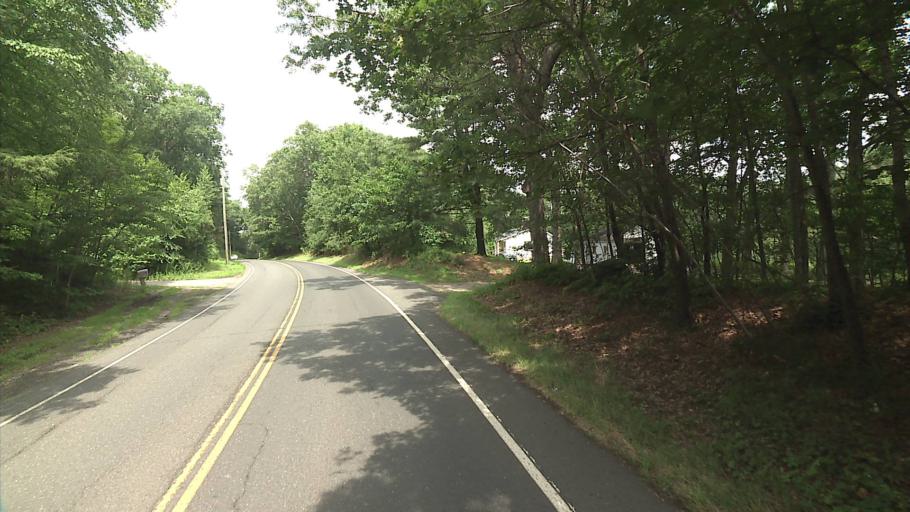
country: US
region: Connecticut
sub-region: New Haven County
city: Oxford
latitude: 41.4592
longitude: -73.1532
